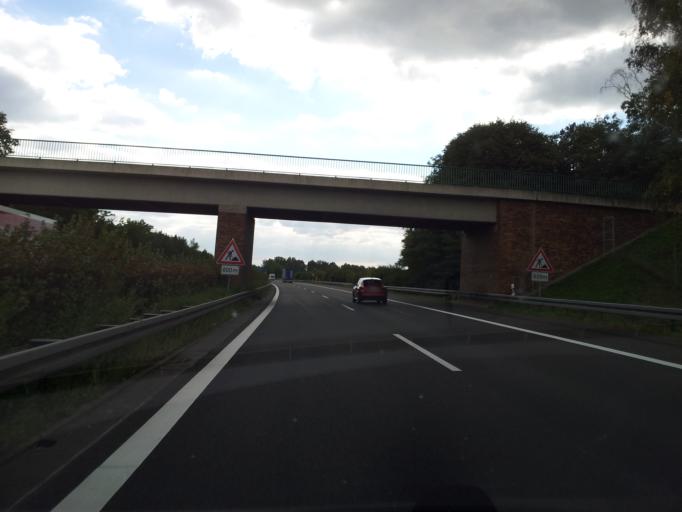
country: DE
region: Brandenburg
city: Schipkau
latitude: 51.5499
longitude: 13.9112
